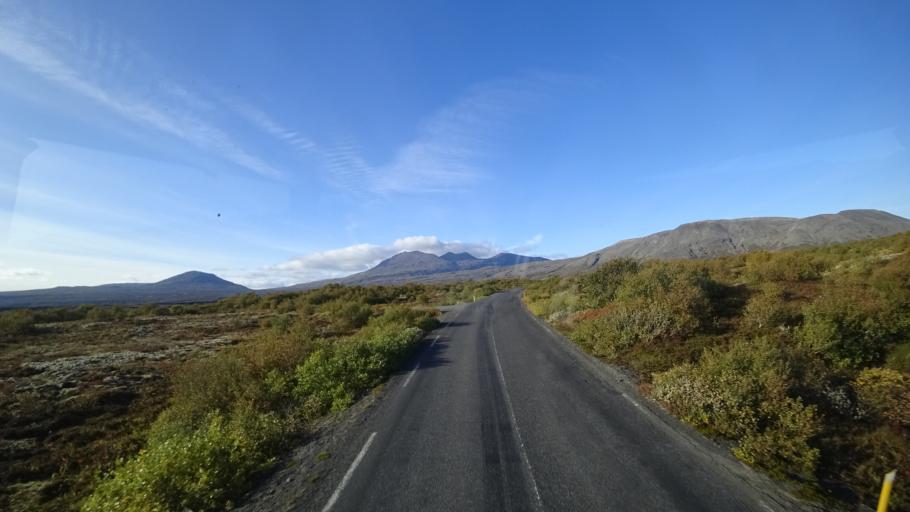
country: IS
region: South
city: Hveragerdi
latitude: 64.2745
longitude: -21.0739
